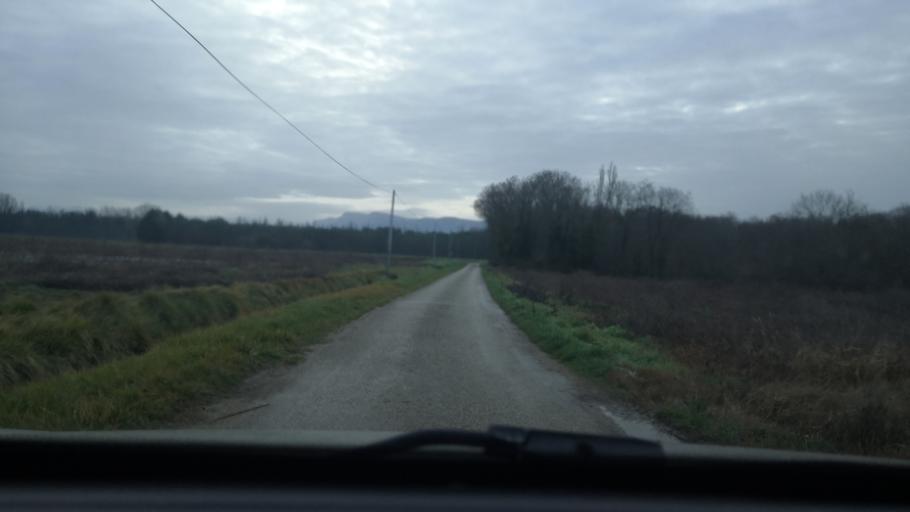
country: FR
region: Rhone-Alpes
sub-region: Departement de la Drome
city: La Begude-de-Mazenc
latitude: 44.5657
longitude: 4.8781
